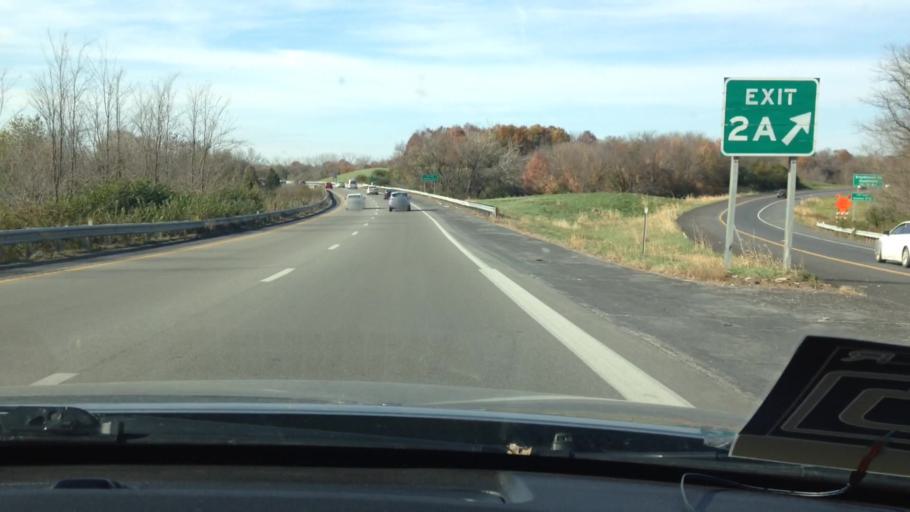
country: US
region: Missouri
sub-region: Platte County
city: Riverside
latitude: 39.1825
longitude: -94.5888
